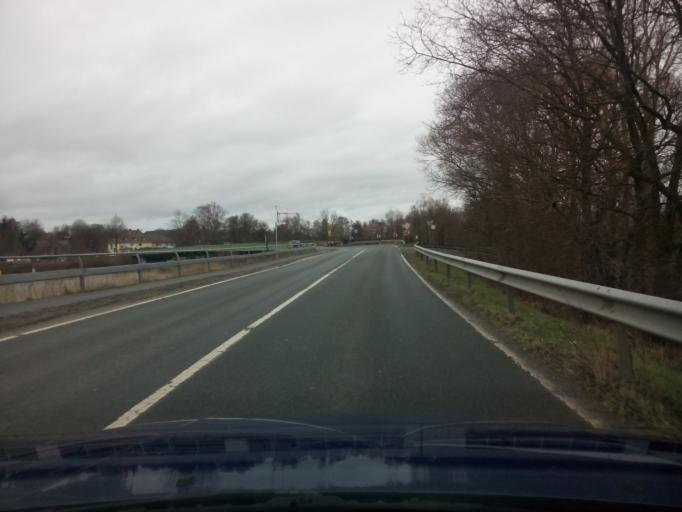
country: DE
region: Lower Saxony
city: Ritterhude
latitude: 53.1753
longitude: 8.7497
